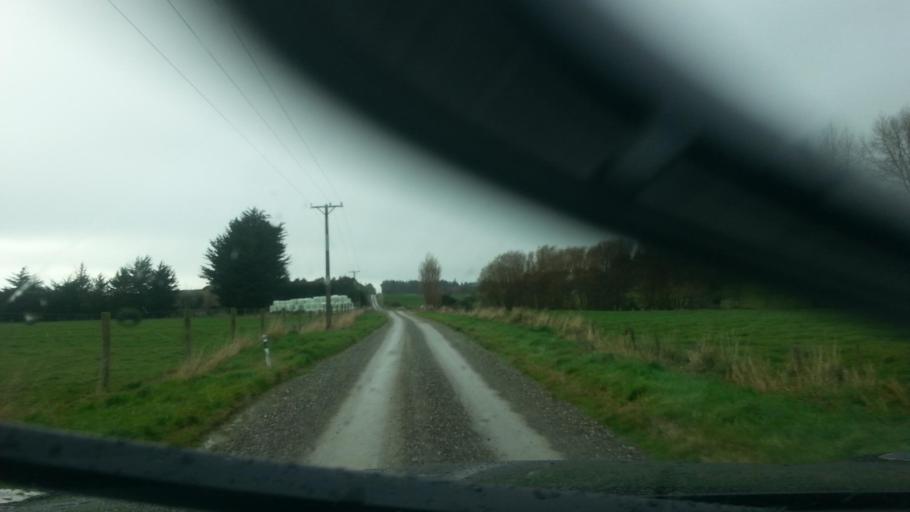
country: NZ
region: Southland
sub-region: Invercargill City
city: Invercargill
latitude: -46.3386
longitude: 168.4013
